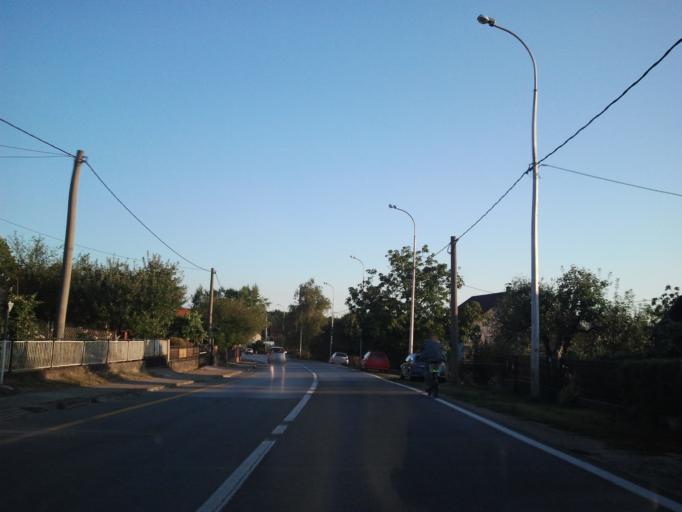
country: HR
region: Sisacko-Moslavacka
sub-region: Grad Sisak
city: Sisak
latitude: 45.4474
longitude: 16.3685
